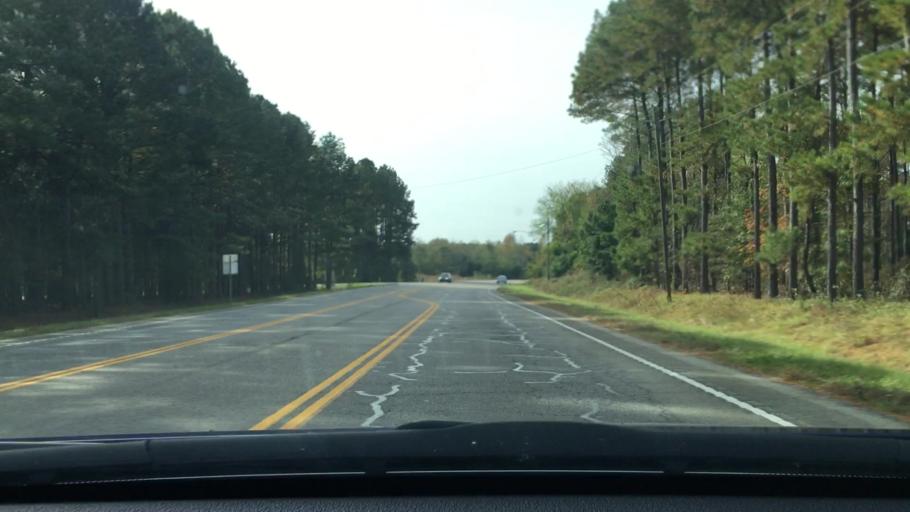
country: US
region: South Carolina
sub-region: Sumter County
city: Cherryvale
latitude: 33.9366
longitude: -80.4407
